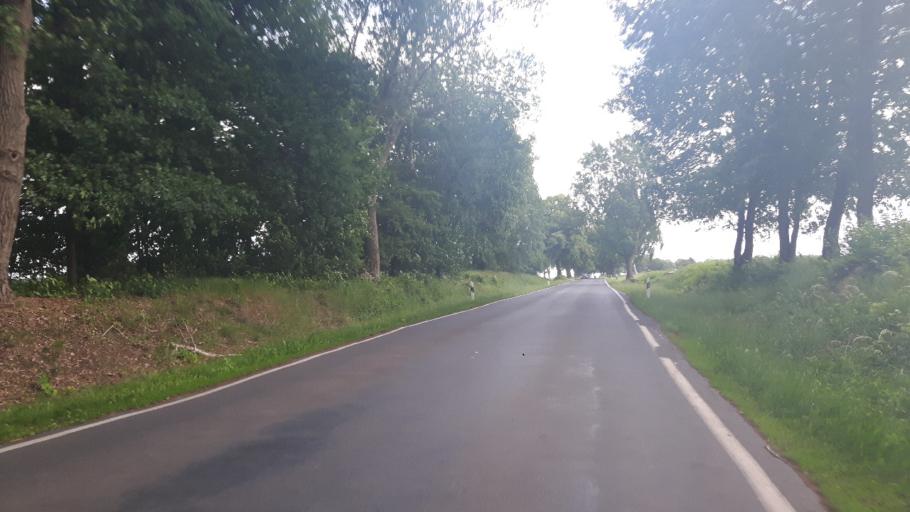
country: DE
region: Brandenburg
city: Bernau bei Berlin
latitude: 52.6467
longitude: 13.5699
